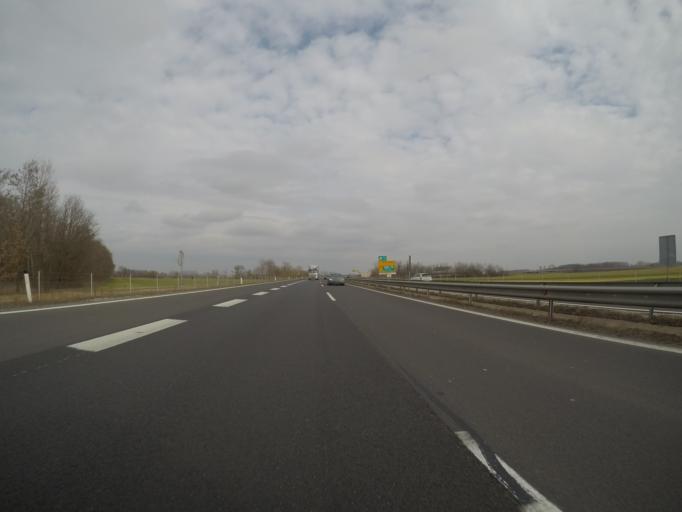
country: SI
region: Murska Sobota
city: Krog
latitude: 46.6327
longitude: 16.1505
